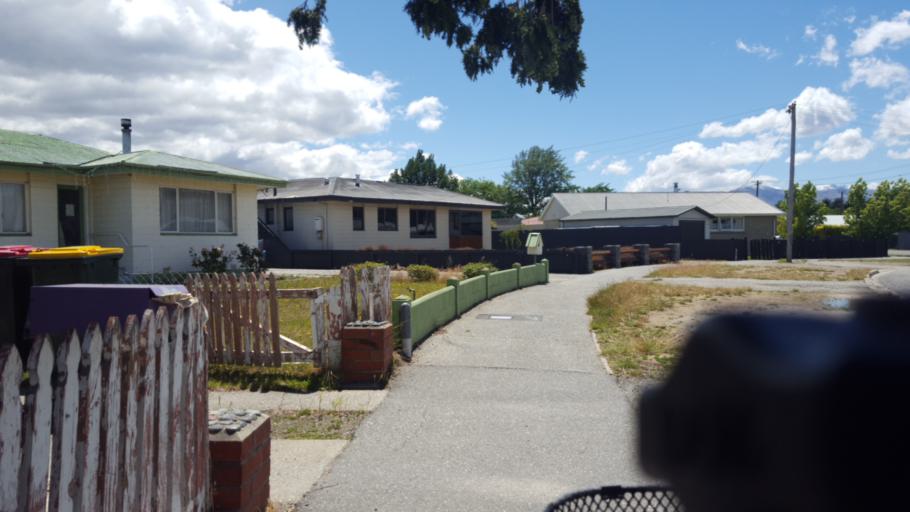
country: NZ
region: Otago
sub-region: Queenstown-Lakes District
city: Wanaka
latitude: -45.2465
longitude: 169.3890
